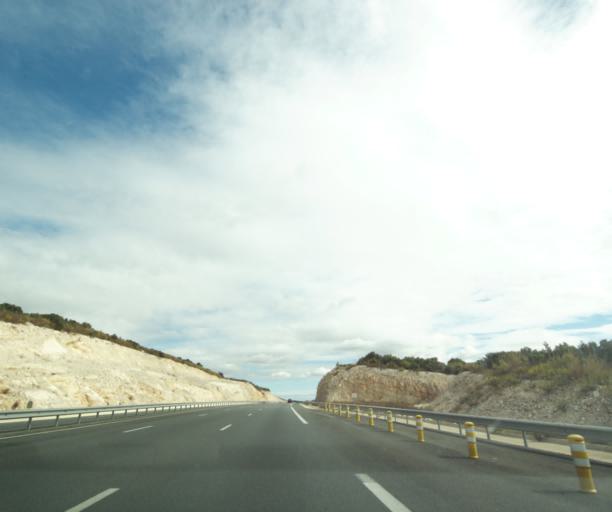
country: FR
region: Languedoc-Roussillon
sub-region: Departement de l'Herault
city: Aniane
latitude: 43.6253
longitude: 3.6154
